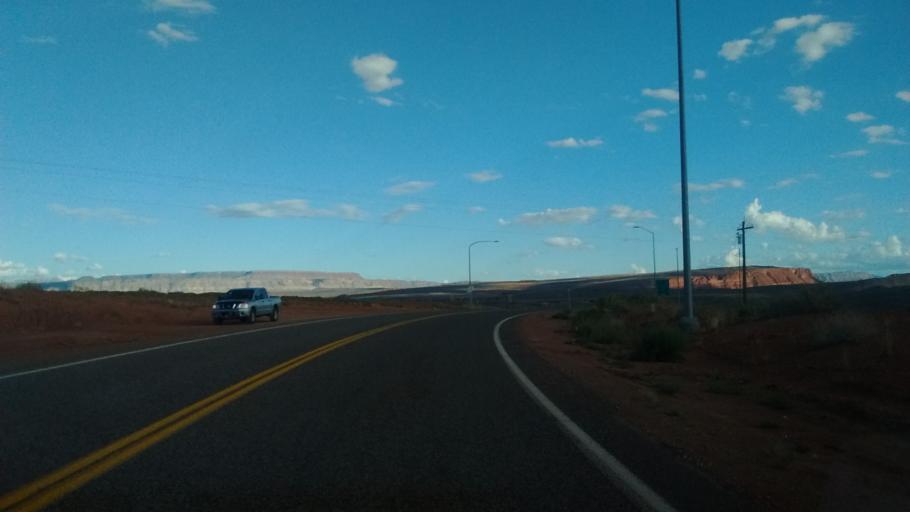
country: US
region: Utah
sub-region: Washington County
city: Washington
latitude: 37.1492
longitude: -113.4895
